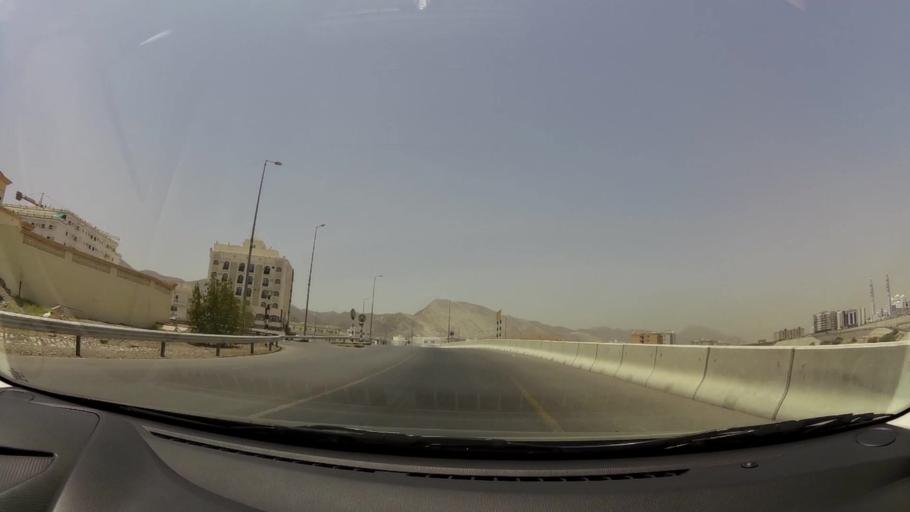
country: OM
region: Muhafazat Masqat
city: Bawshar
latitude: 23.5837
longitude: 58.4217
